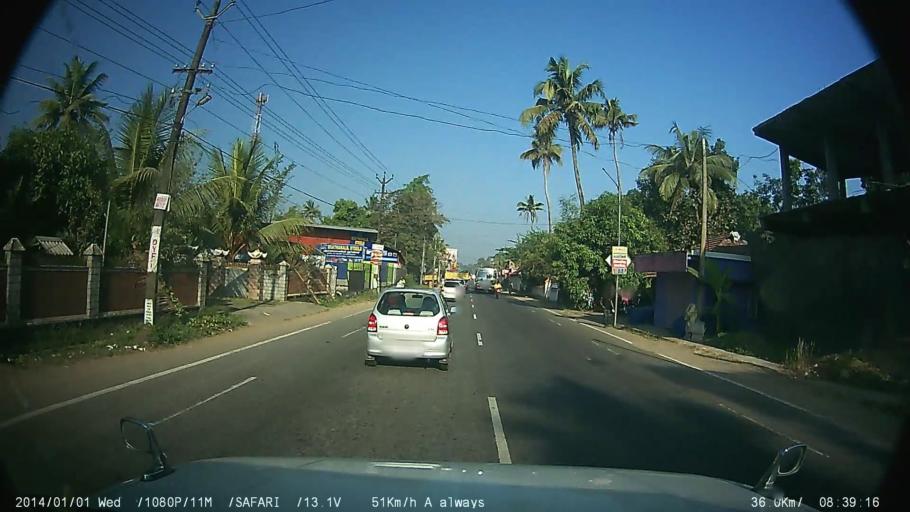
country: IN
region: Kerala
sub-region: Ernakulam
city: Perumpavur
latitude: 10.1550
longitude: 76.4478
